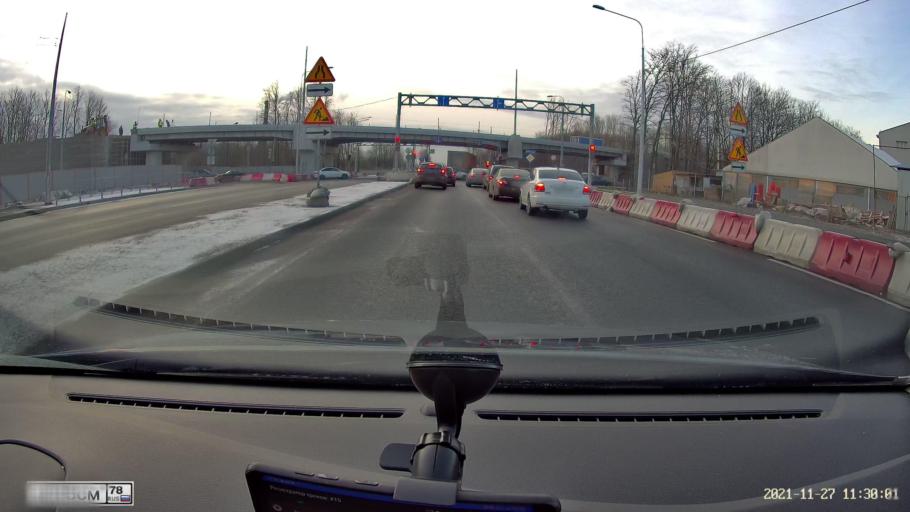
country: RU
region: St.-Petersburg
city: Krasnoye Selo
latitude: 59.7309
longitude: 30.0575
